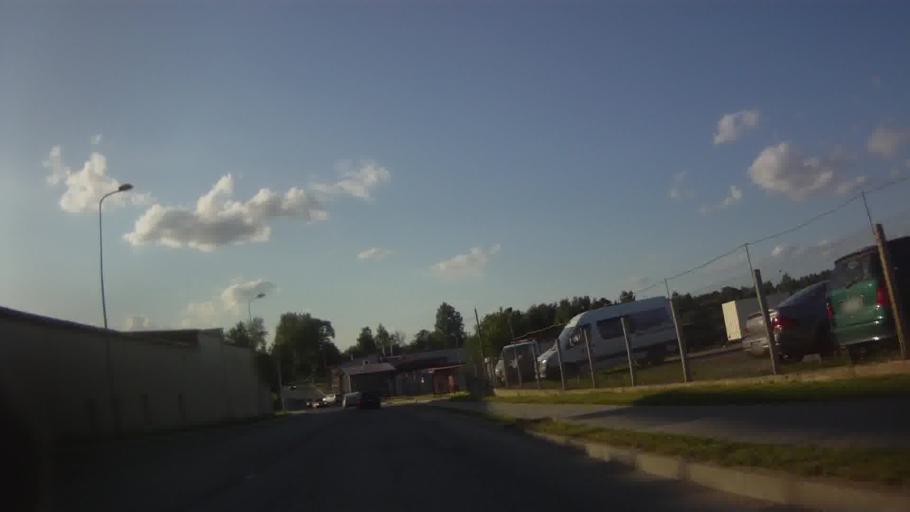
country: LV
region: Rezekne
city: Rezekne
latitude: 56.5126
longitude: 27.3247
